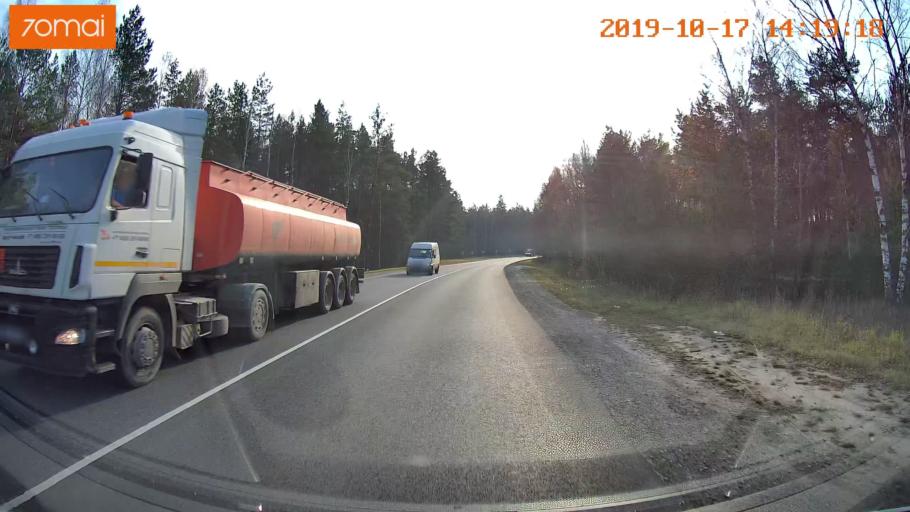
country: RU
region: Rjazan
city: Spas-Klepiki
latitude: 55.0516
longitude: 40.0230
